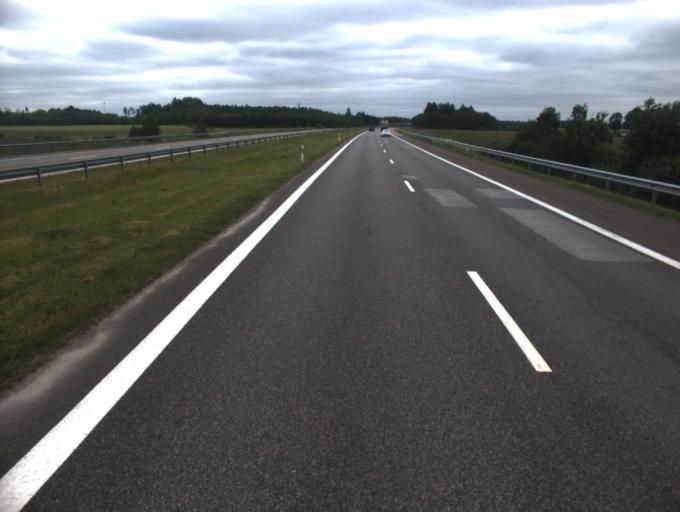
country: LT
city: Rietavas
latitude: 55.6303
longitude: 21.9583
